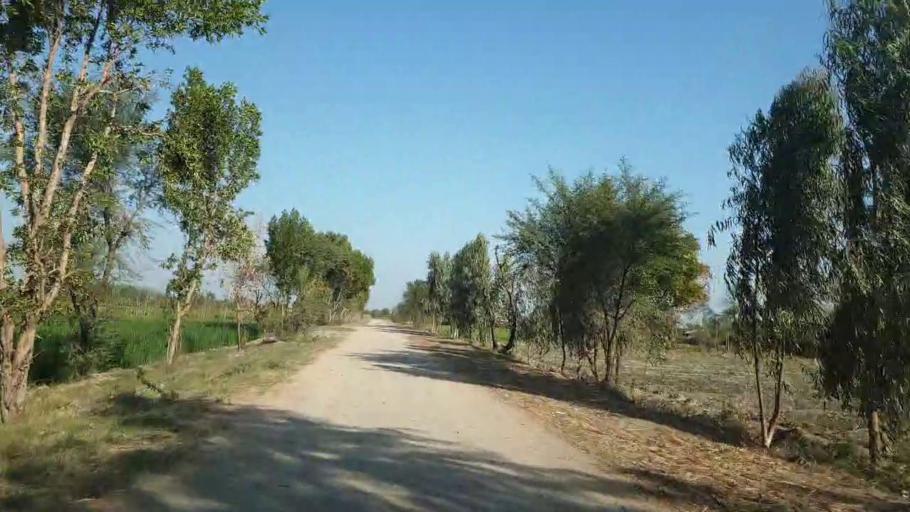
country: PK
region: Sindh
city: Mirpur Khas
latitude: 25.6284
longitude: 69.0661
